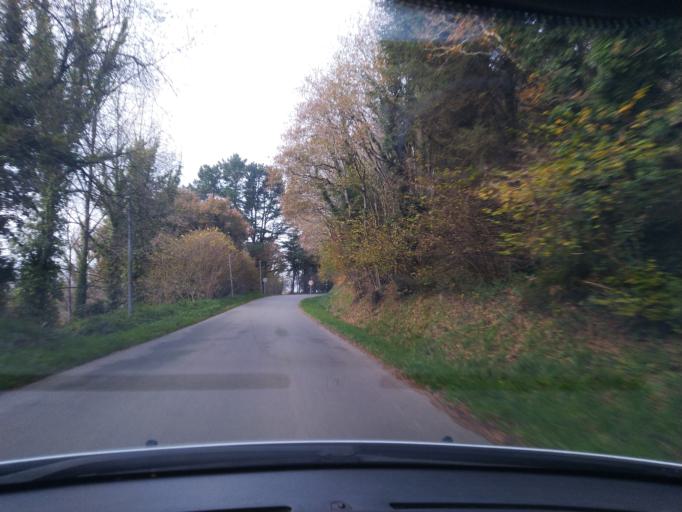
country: FR
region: Brittany
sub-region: Departement du Finistere
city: Guerlesquin
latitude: 48.5351
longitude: -3.6134
